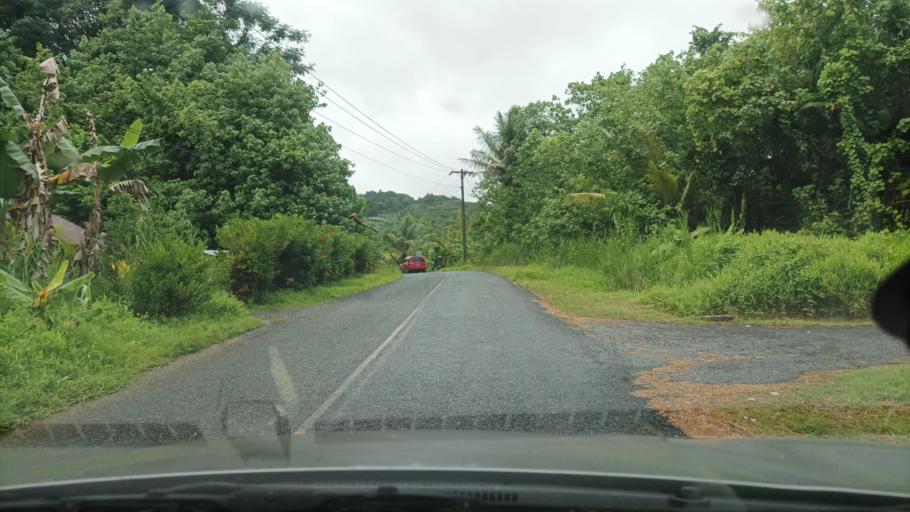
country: FM
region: Pohnpei
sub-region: Madolenihm Municipality
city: Madolenihm Municipality Government
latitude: 6.8090
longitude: 158.2628
